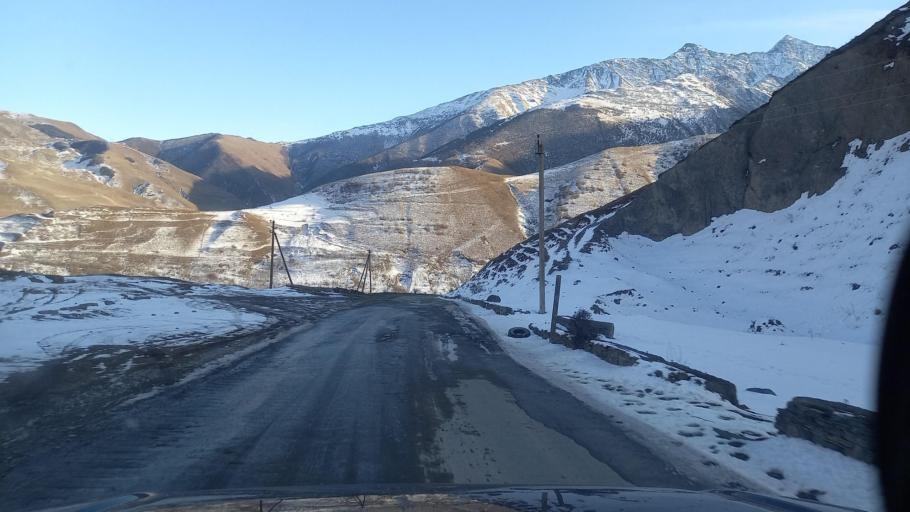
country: RU
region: Ingushetiya
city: Dzhayrakh
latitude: 42.8440
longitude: 44.5096
